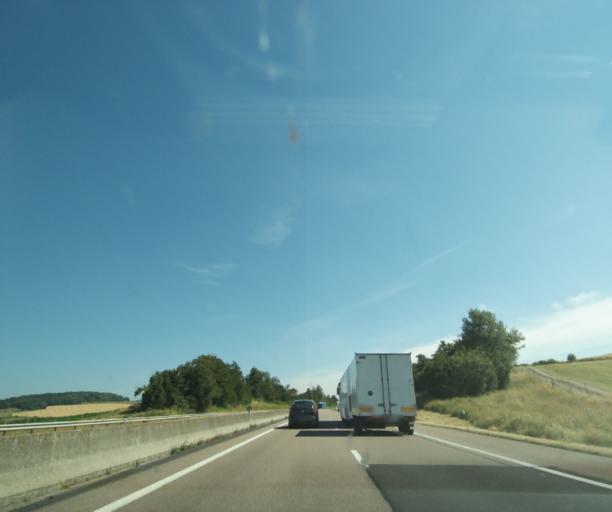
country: FR
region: Lorraine
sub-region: Departement des Vosges
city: Chatenois
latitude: 48.3659
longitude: 5.8683
